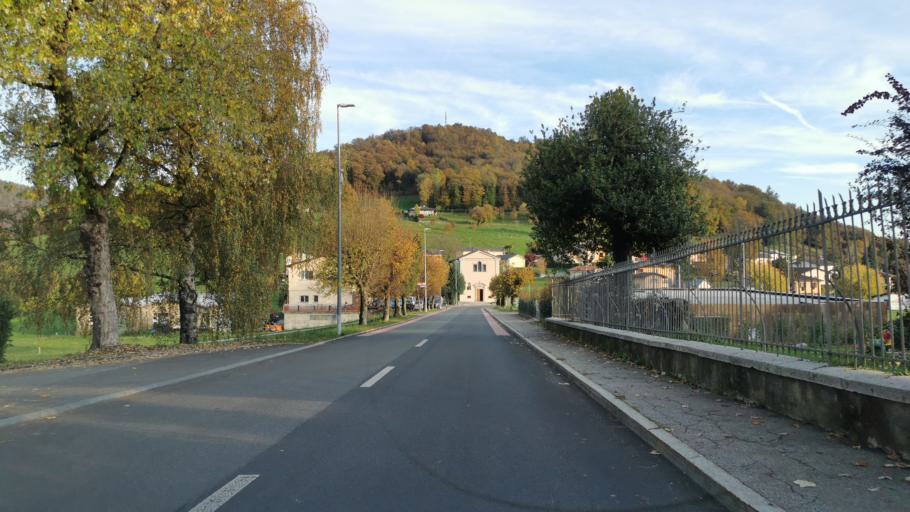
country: CH
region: Ticino
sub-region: Lugano District
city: Pura
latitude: 46.0097
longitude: 8.8574
